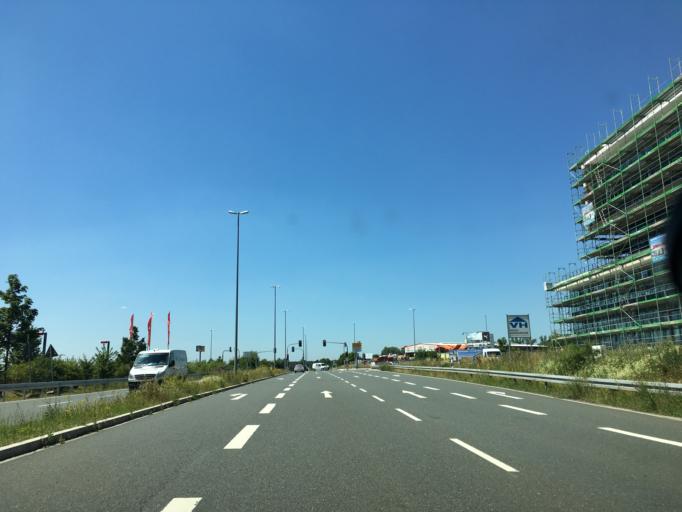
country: DE
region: Bavaria
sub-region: Regierungsbezirk Mittelfranken
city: Herzogenaurach
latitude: 49.5751
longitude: 10.9014
